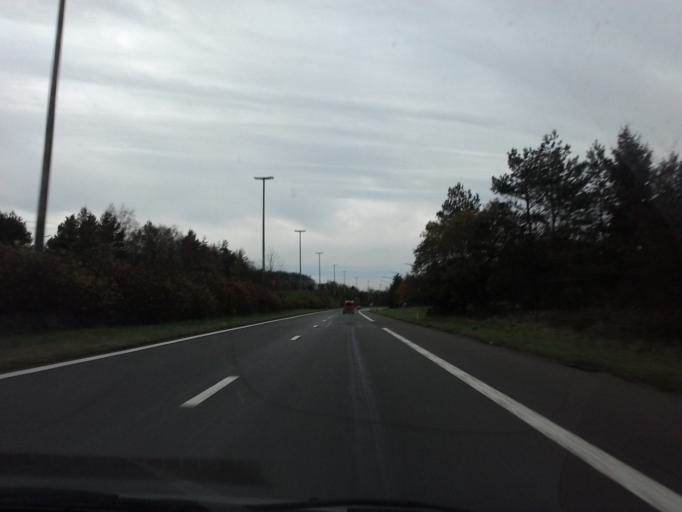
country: BE
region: Wallonia
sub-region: Province de Liege
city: Aywaille
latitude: 50.4280
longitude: 5.7007
